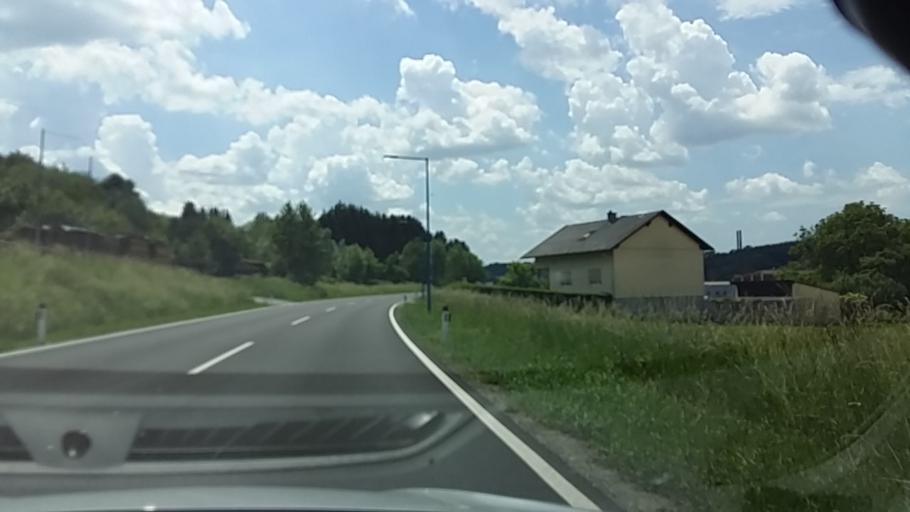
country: AT
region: Burgenland
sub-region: Politischer Bezirk Gussing
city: Stegersbach
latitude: 47.1731
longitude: 16.1660
